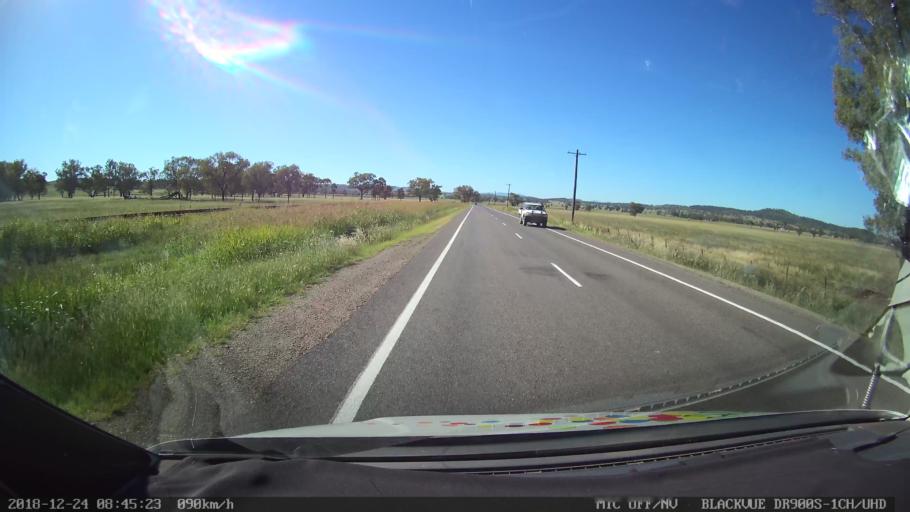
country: AU
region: New South Wales
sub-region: Liverpool Plains
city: Quirindi
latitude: -31.4142
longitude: 150.6518
